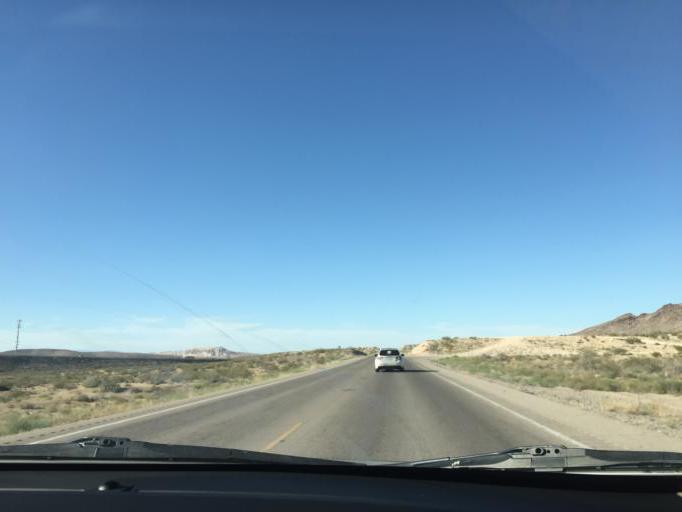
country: US
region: Nevada
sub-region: Clark County
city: Enterprise
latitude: 35.8769
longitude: -115.2303
